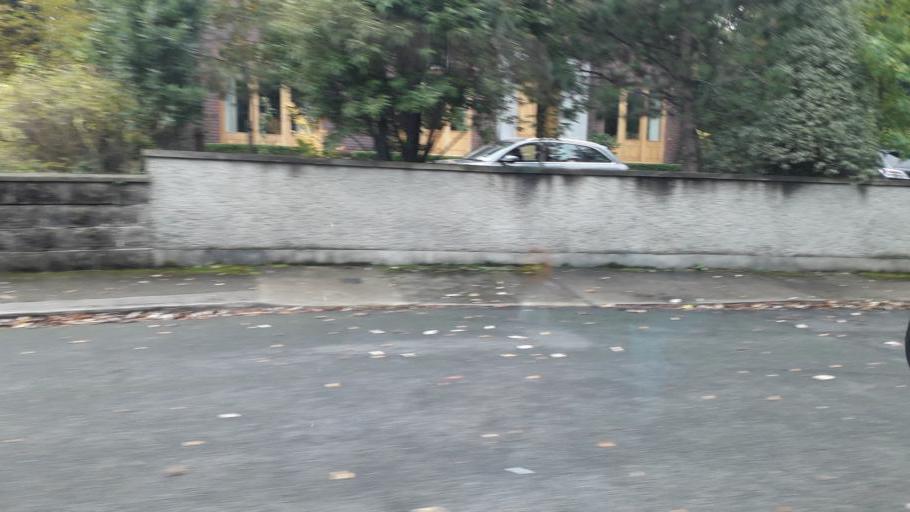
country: IE
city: Milltown
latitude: 53.3110
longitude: -6.2450
